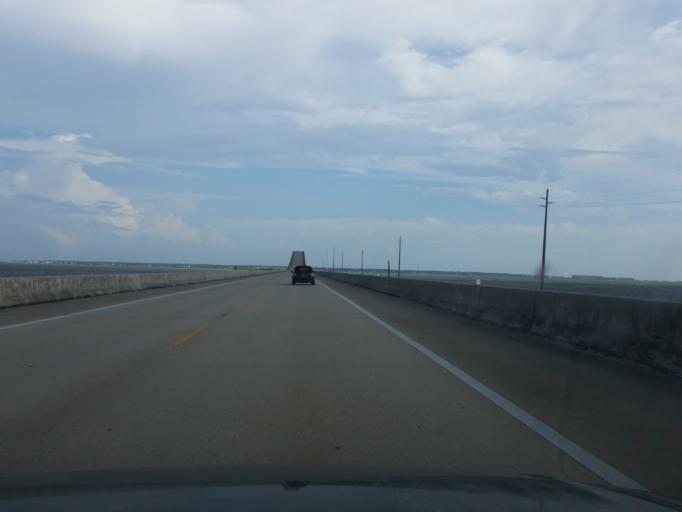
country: US
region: Alabama
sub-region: Mobile County
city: Dauphin Island
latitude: 30.2980
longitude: -88.1333
